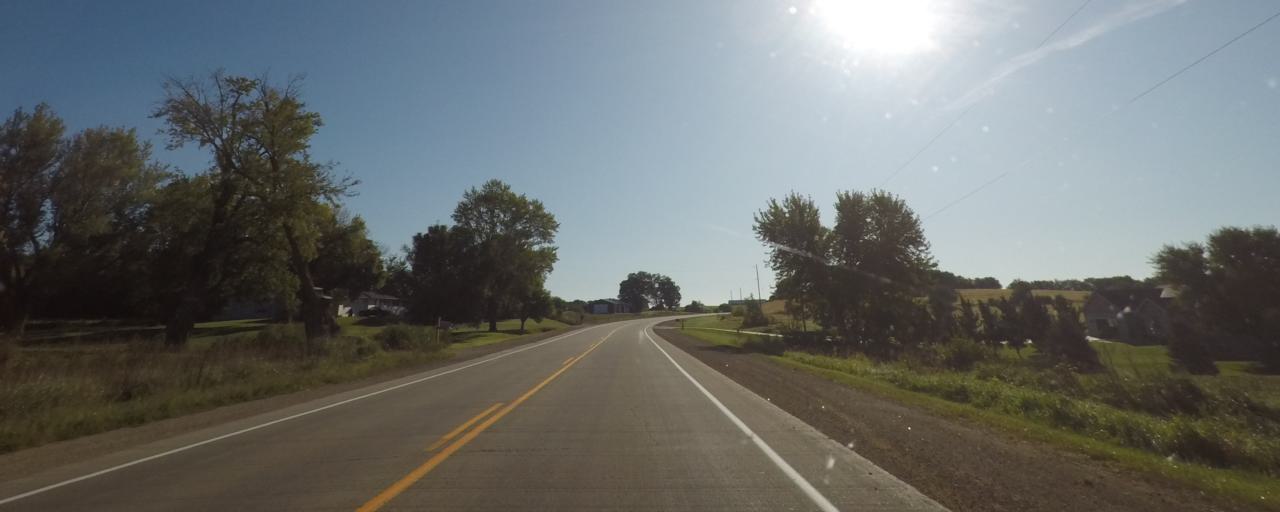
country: US
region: Wisconsin
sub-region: Dane County
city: Deerfield
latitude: 43.0368
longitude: -89.0990
